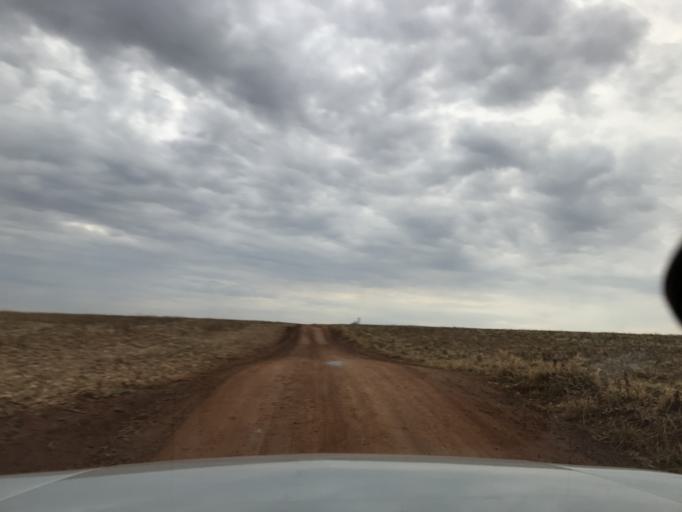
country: BR
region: Parana
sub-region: Palotina
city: Palotina
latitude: -24.2206
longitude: -53.8350
